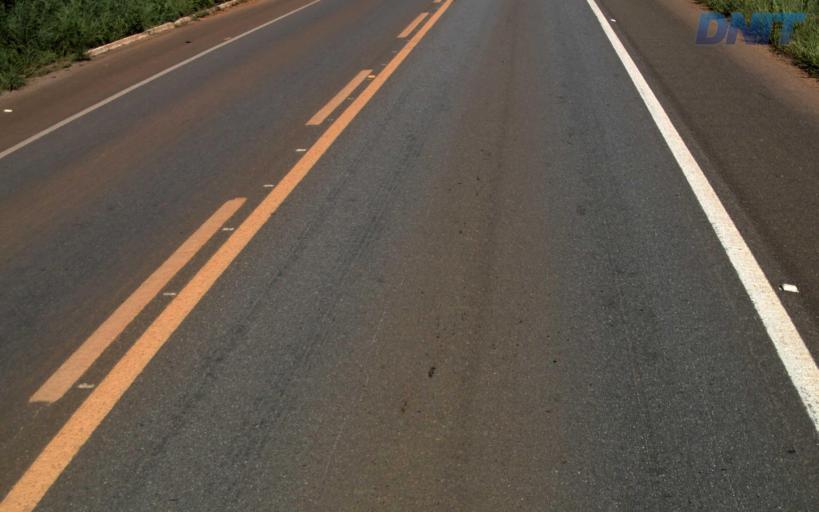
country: BR
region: Goias
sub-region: Barro Alto
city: Barro Alto
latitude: -15.2091
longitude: -48.6950
